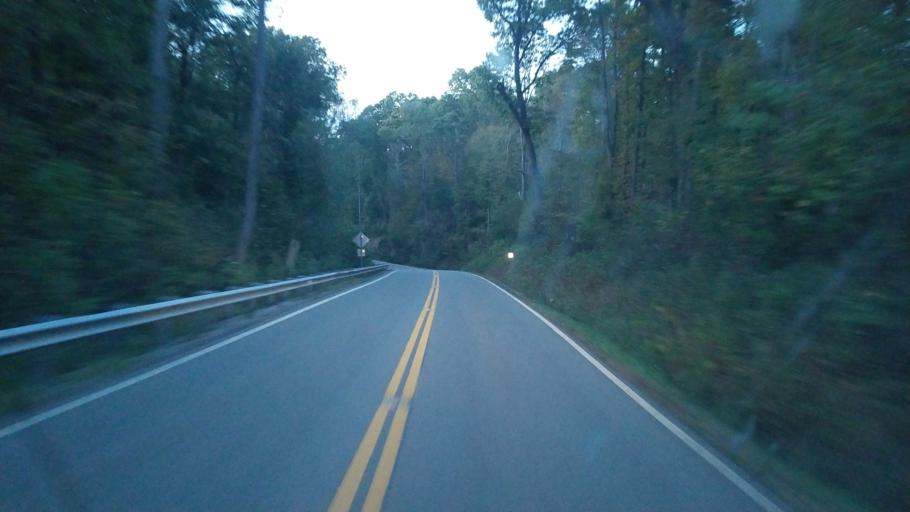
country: US
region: Ohio
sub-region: Meigs County
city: Pomeroy
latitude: 39.1067
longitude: -82.1035
